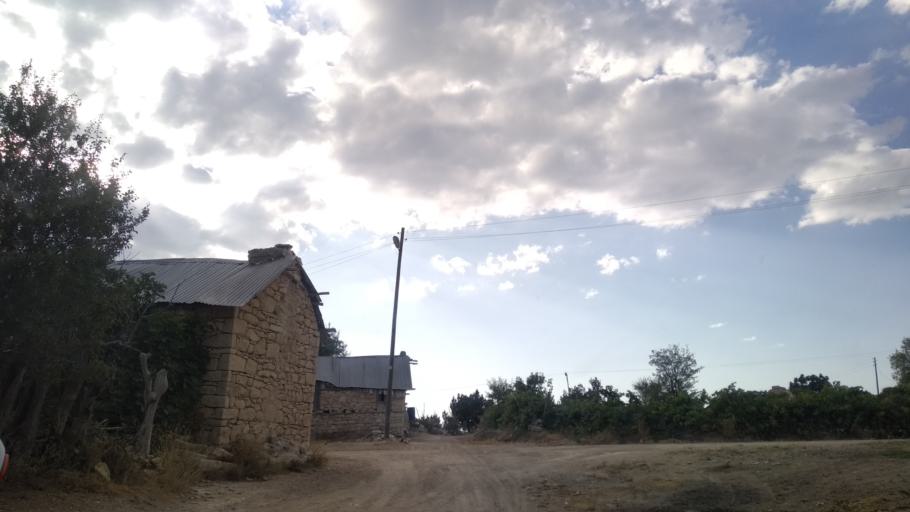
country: TR
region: Mersin
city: Sarikavak
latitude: 36.6012
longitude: 33.7240
